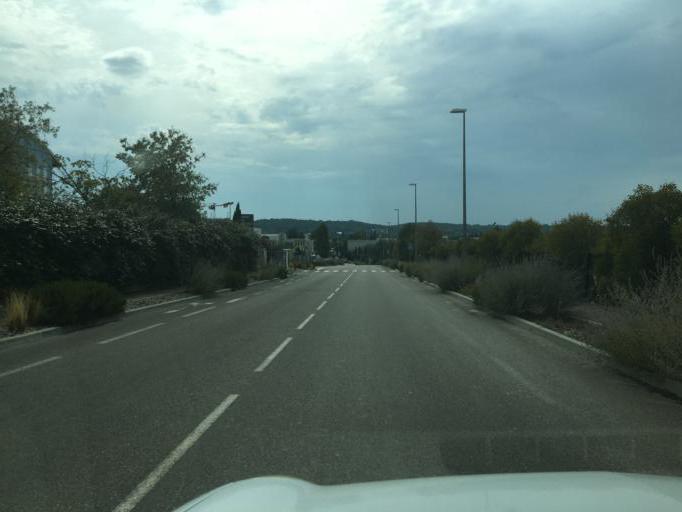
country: FR
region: Provence-Alpes-Cote d'Azur
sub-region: Departement des Bouches-du-Rhone
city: Bouc-Bel-Air
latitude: 43.4849
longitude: 5.3891
